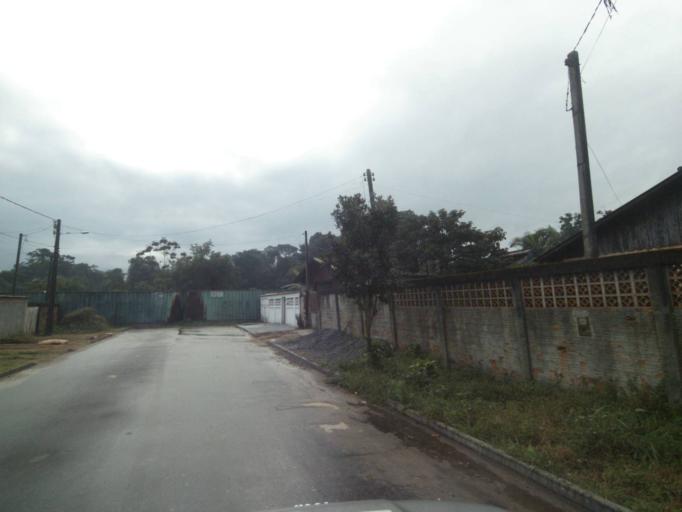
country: BR
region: Parana
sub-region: Paranagua
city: Paranagua
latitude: -25.5601
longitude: -48.5662
